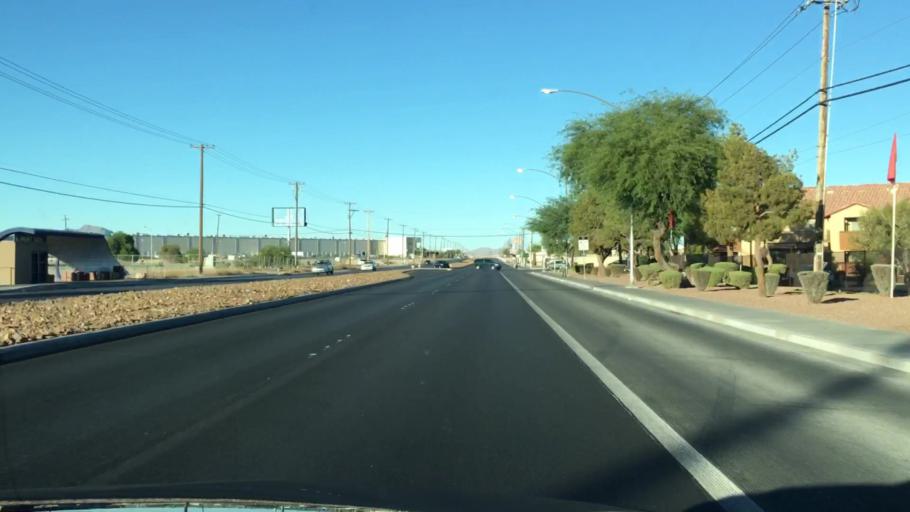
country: US
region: Nevada
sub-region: Clark County
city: Sunrise Manor
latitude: 36.2192
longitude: -115.0907
